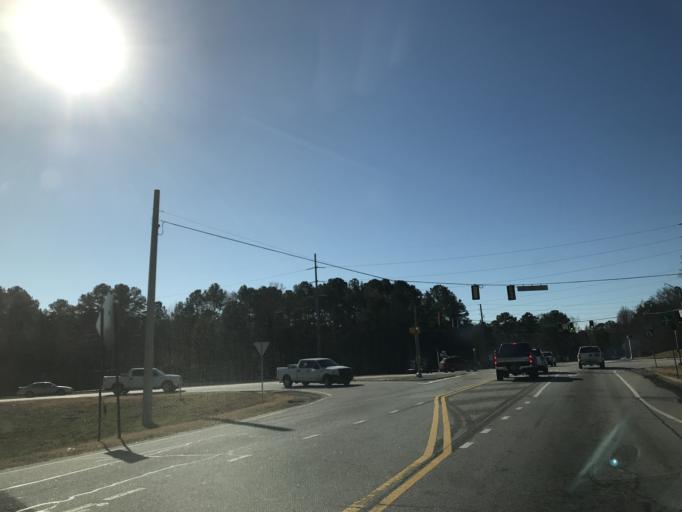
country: US
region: Georgia
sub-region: Paulding County
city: Dallas
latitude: 33.9160
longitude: -84.8563
